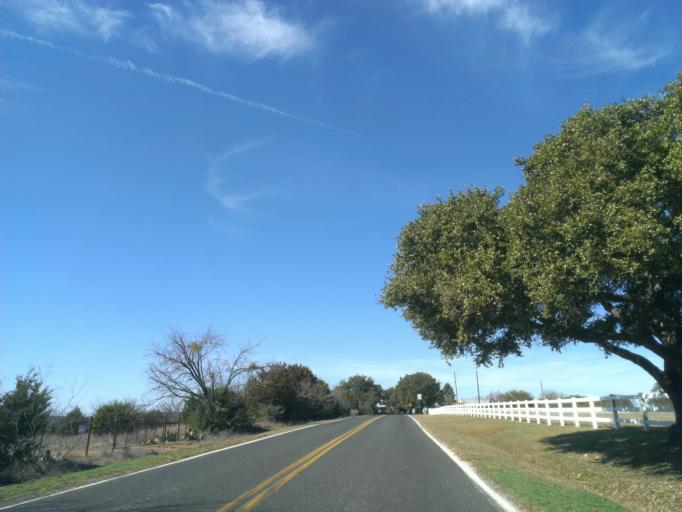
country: US
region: Texas
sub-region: Travis County
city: Briarcliff
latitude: 30.4484
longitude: -98.0740
